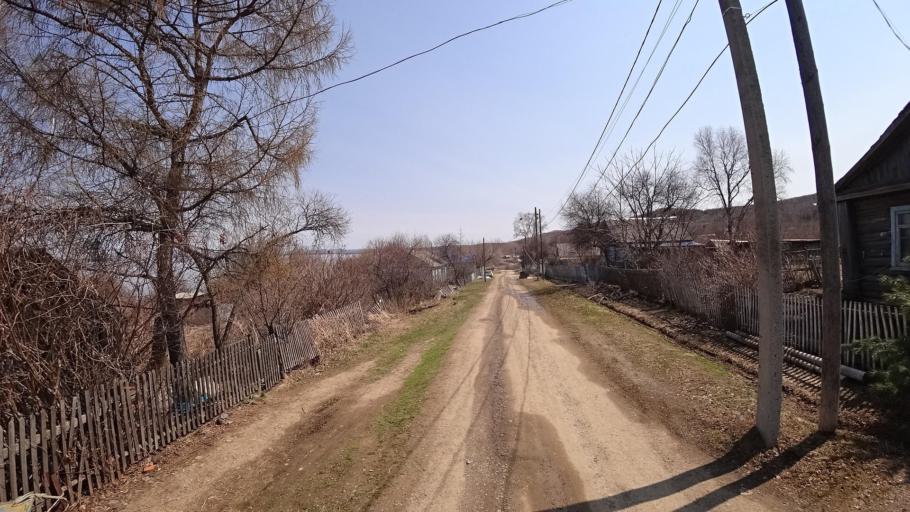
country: RU
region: Khabarovsk Krai
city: Selikhino
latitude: 50.6701
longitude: 137.3976
